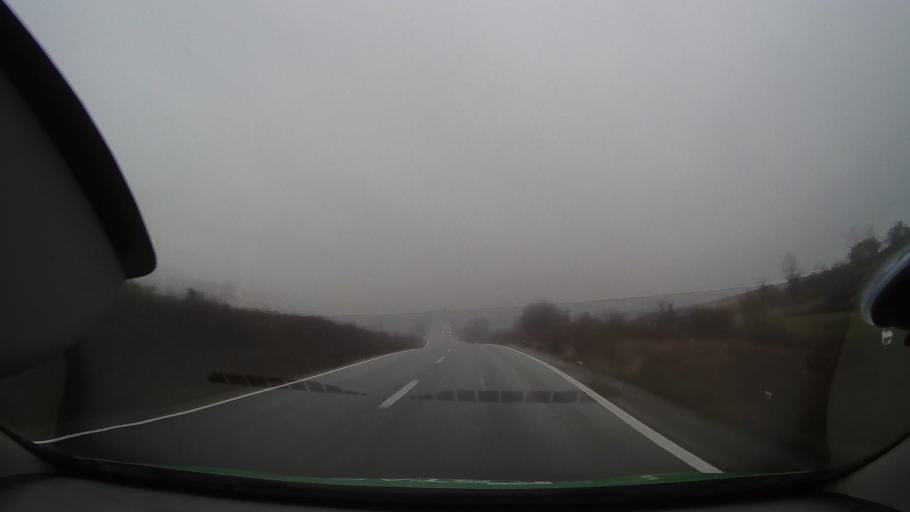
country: RO
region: Bihor
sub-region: Comuna Olcea
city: Olcea
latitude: 46.6807
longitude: 21.9661
